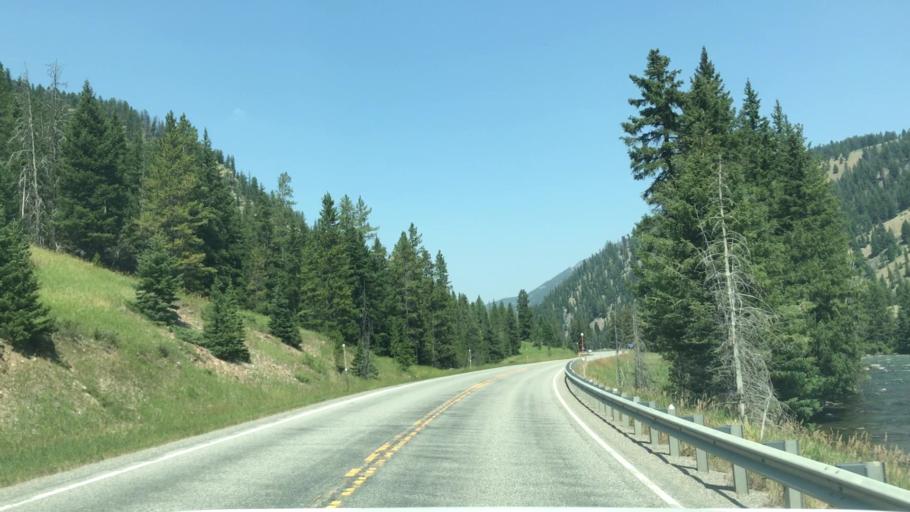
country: US
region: Montana
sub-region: Gallatin County
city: Big Sky
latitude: 45.0800
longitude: -111.2082
